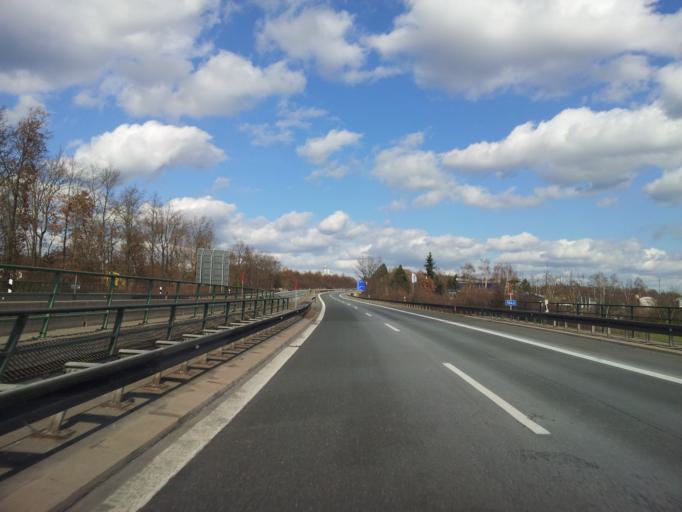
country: DE
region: Bavaria
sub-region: Upper Franconia
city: Thurnau
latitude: 50.0178
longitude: 11.3992
